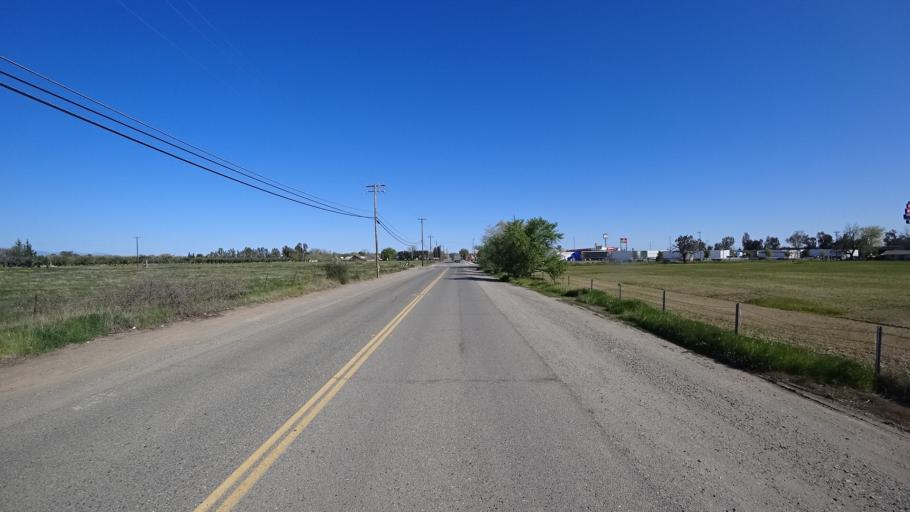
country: US
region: California
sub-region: Glenn County
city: Orland
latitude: 39.7487
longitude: -122.2089
